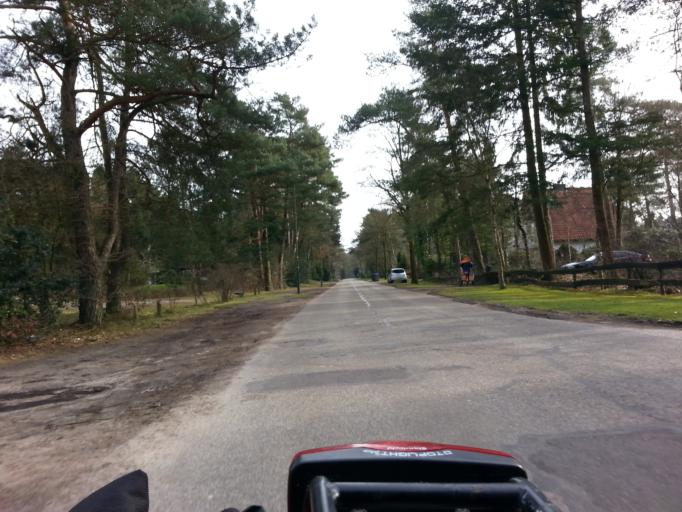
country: NL
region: Utrecht
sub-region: Gemeente Utrechtse Heuvelrug
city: Maarn
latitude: 52.0669
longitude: 5.3684
